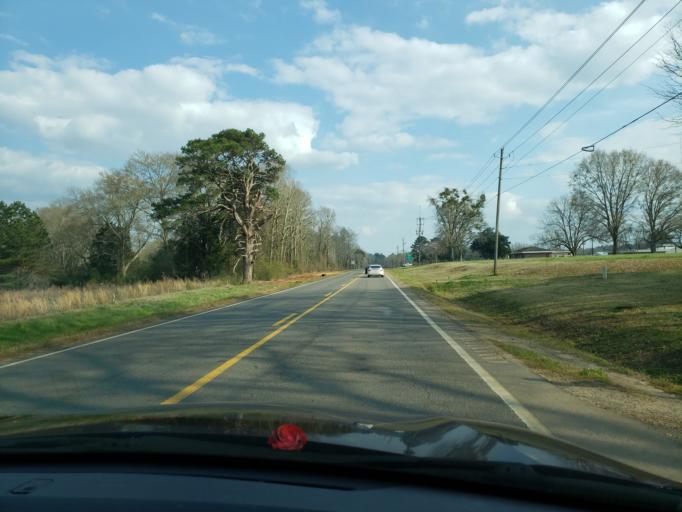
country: US
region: Alabama
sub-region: Hale County
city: Greensboro
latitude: 32.7146
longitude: -87.6166
